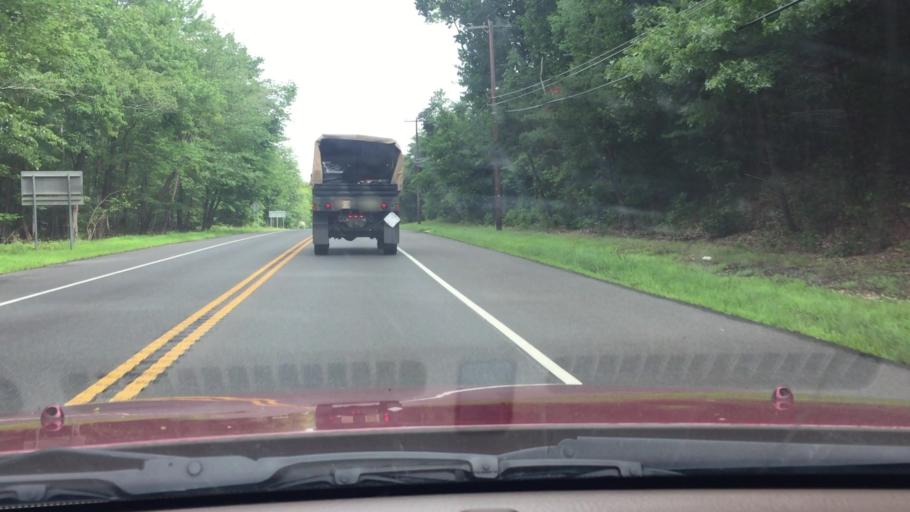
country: US
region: New Jersey
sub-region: Burlington County
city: Fort Dix
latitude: 40.0317
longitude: -74.6418
